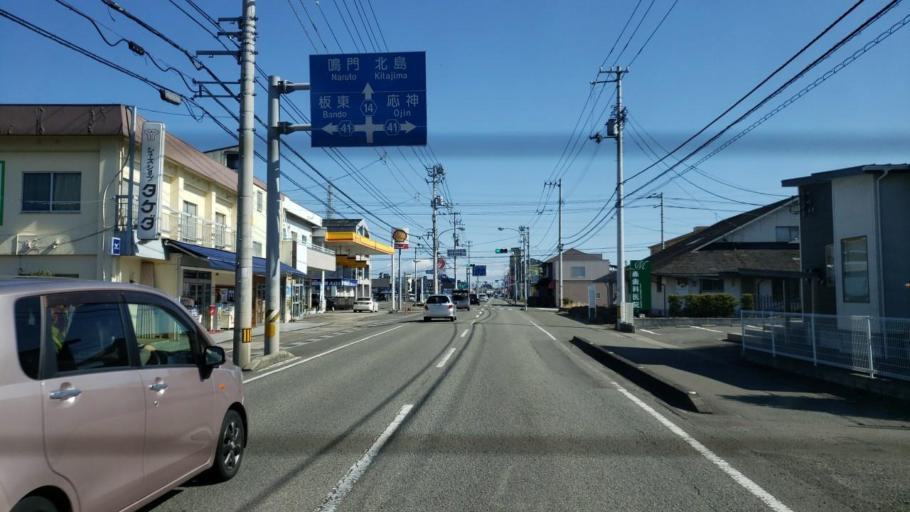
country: JP
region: Tokushima
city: Tokushima-shi
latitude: 34.1326
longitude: 134.5172
